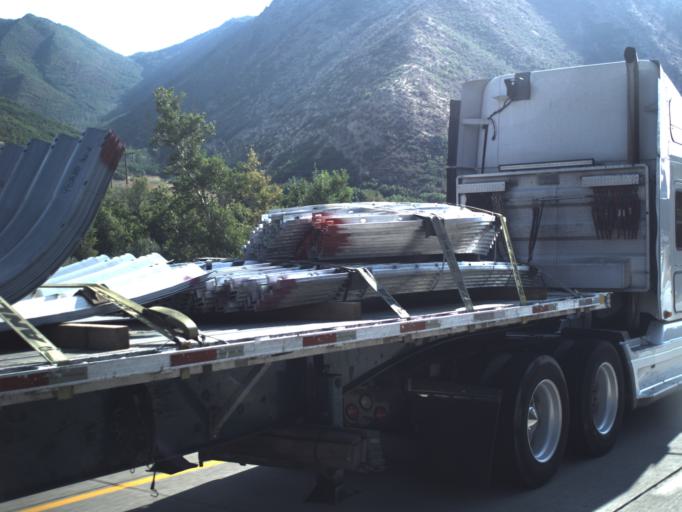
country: US
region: Utah
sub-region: Morgan County
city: Morgan
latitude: 41.0635
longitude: -111.5616
